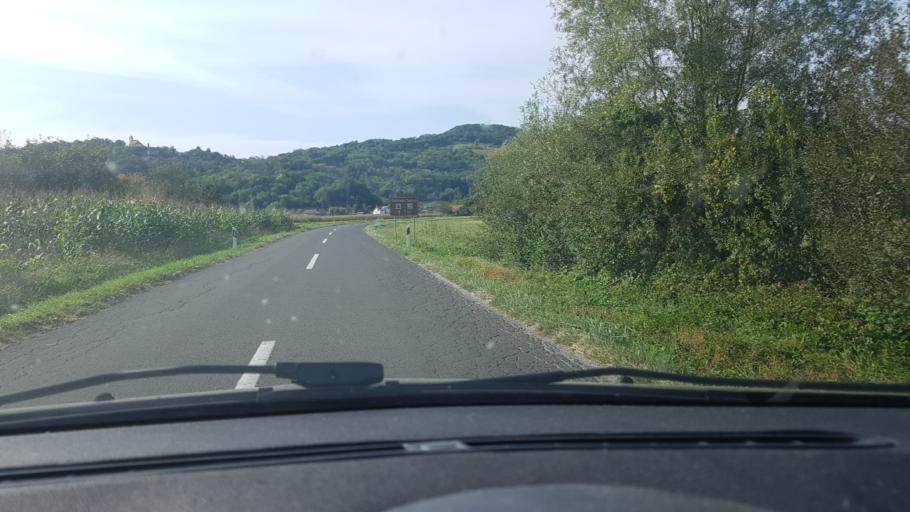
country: HR
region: Krapinsko-Zagorska
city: Zlatar
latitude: 46.1030
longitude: 16.0209
